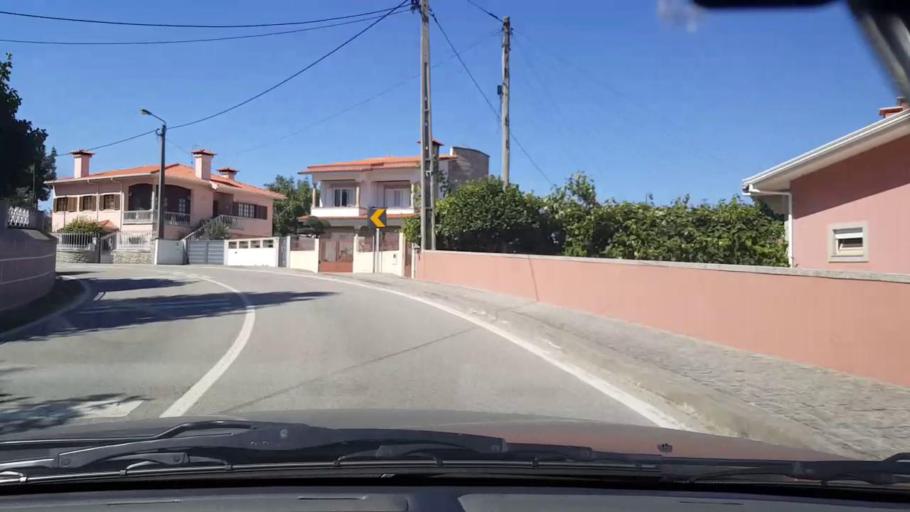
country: PT
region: Porto
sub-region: Maia
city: Gemunde
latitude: 41.3399
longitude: -8.6394
